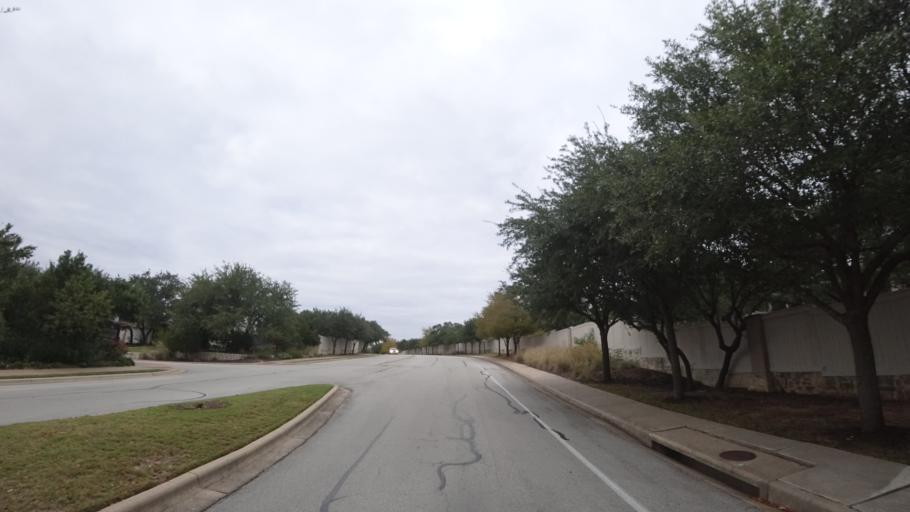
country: US
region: Texas
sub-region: Travis County
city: Bee Cave
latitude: 30.3120
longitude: -97.9186
